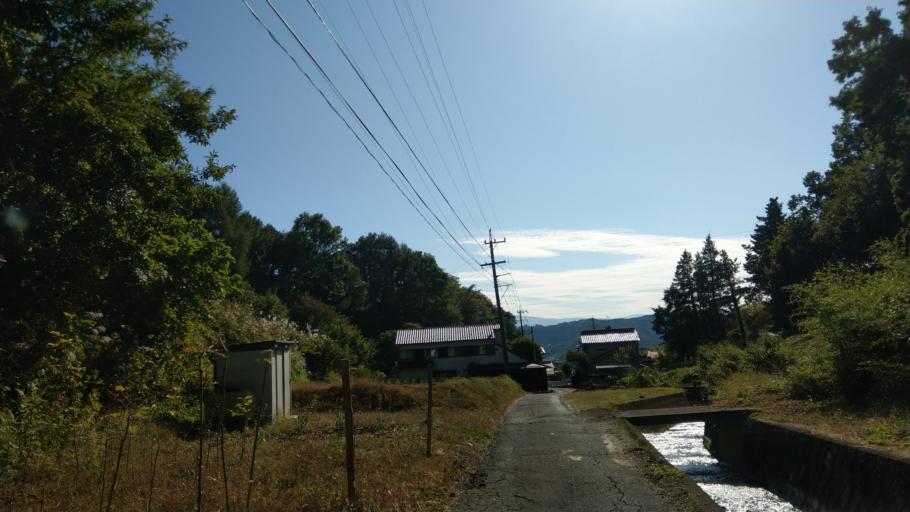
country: JP
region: Nagano
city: Komoro
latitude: 36.3358
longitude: 138.4330
